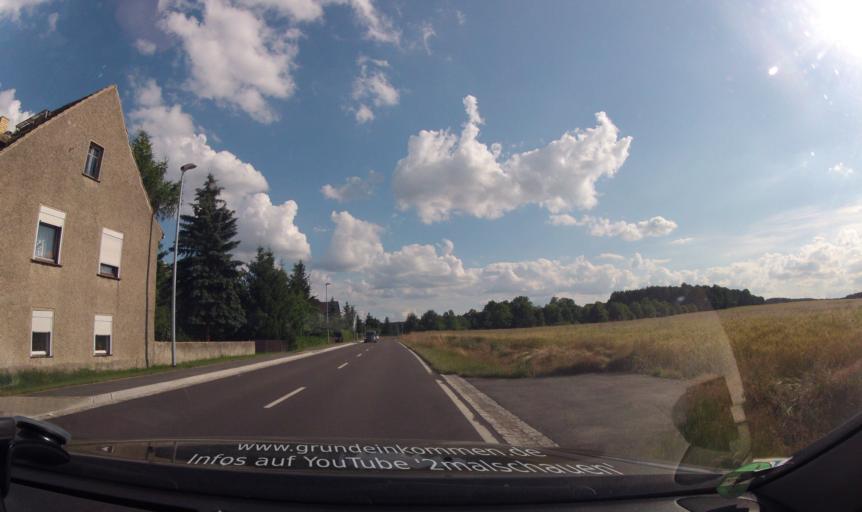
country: DE
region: Saxony
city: Schildau
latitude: 51.4422
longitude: 12.9274
